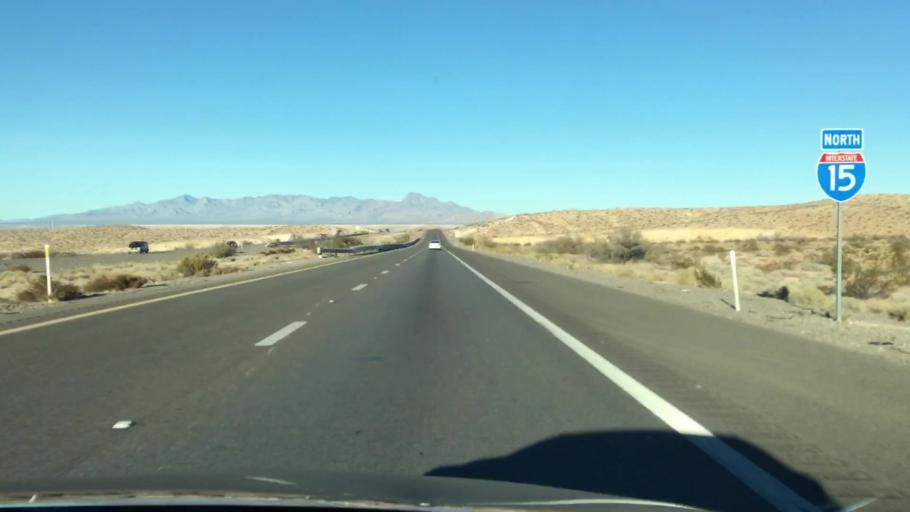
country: US
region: Nevada
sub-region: Clark County
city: Moapa Town
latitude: 36.5926
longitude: -114.6455
